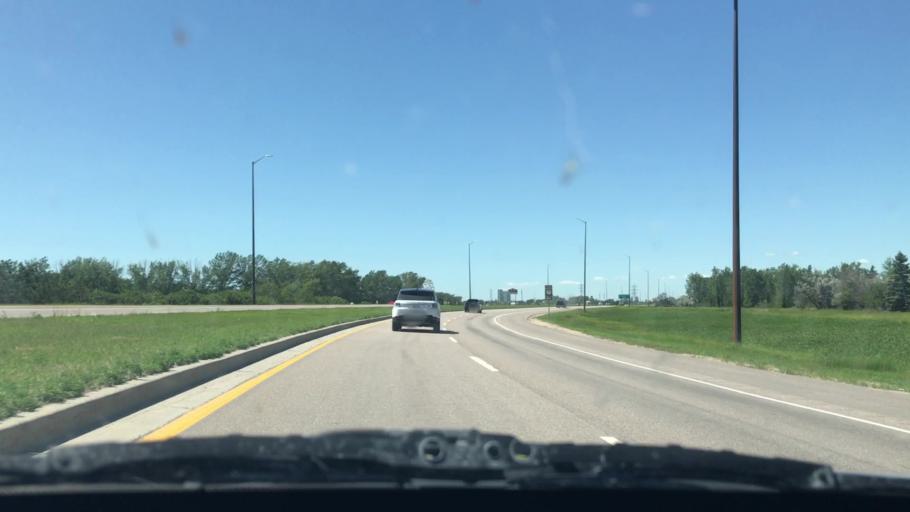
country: CA
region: Manitoba
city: Winnipeg
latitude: 49.8362
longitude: -96.9735
